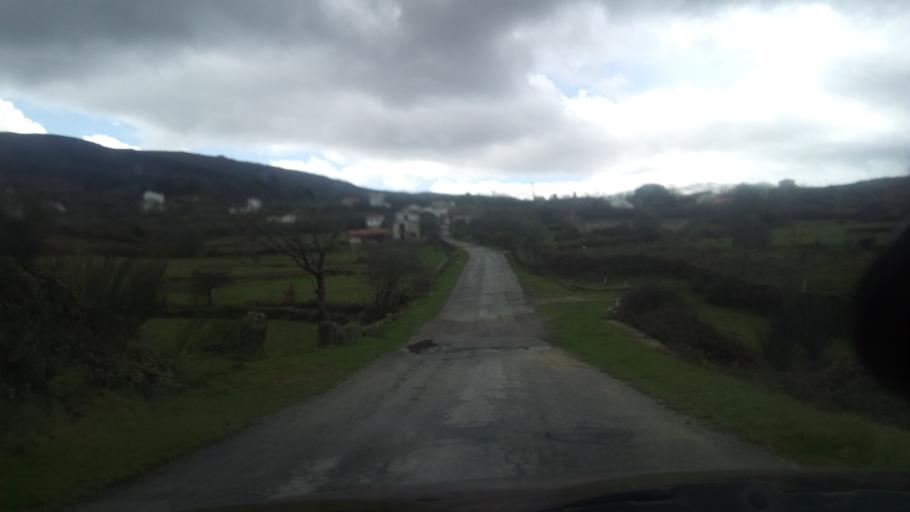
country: PT
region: Guarda
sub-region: Celorico da Beira
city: Celorico da Beira
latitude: 40.5599
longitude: -7.4569
